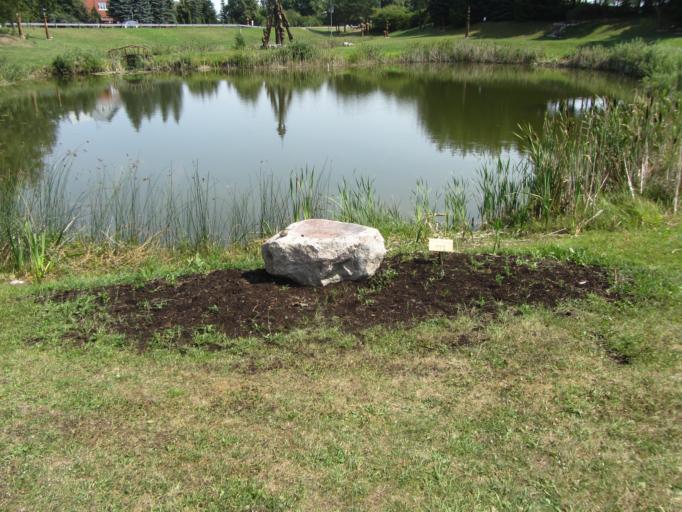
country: LT
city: Veisiejai
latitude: 54.1044
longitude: 23.6748
